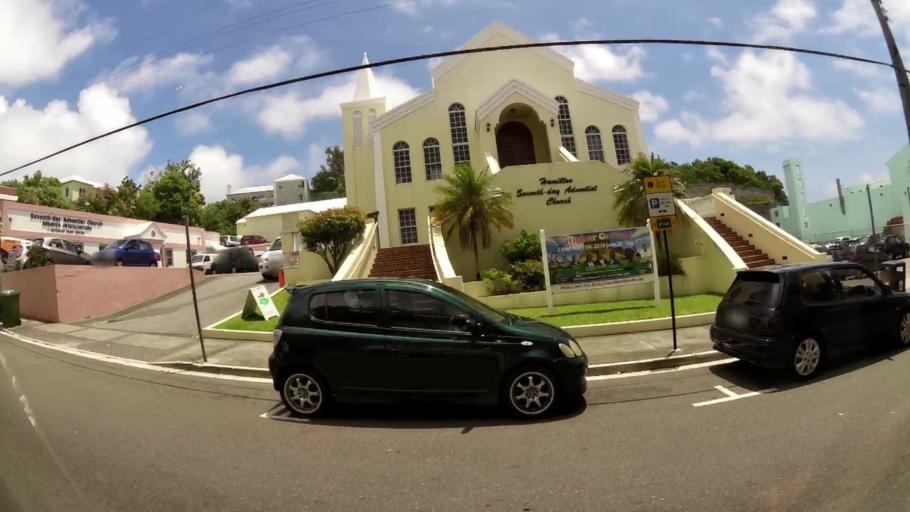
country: BM
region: Hamilton city
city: Hamilton
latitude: 32.2947
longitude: -64.7789
